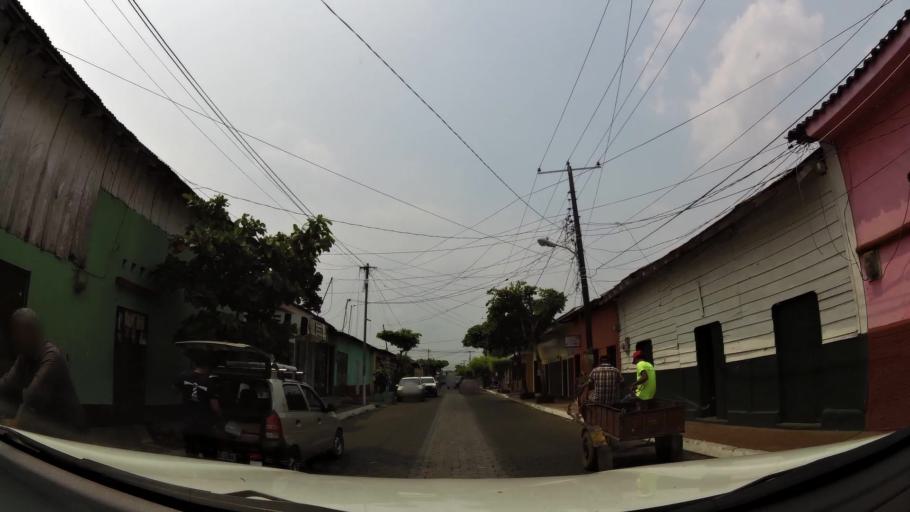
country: NI
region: Chinandega
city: Chinandega
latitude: 12.6273
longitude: -87.1354
